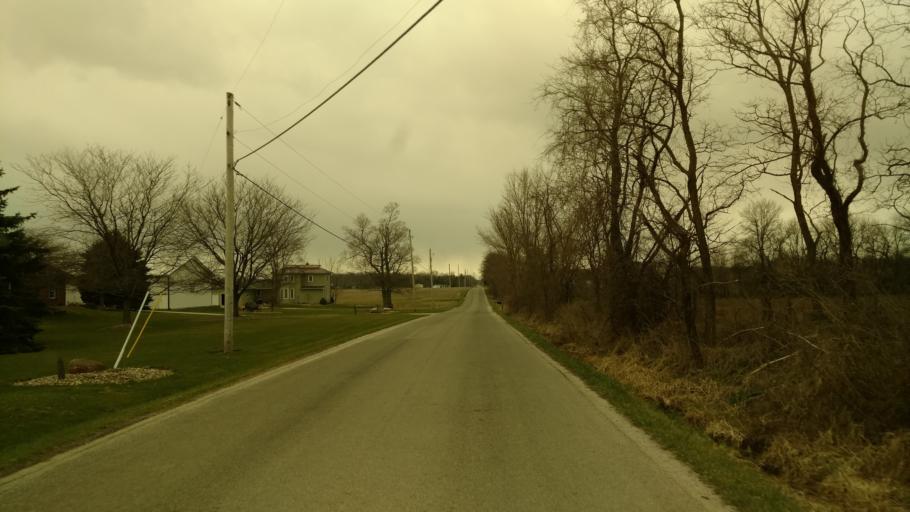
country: US
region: Ohio
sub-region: Crawford County
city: Galion
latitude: 40.6615
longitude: -82.7844
